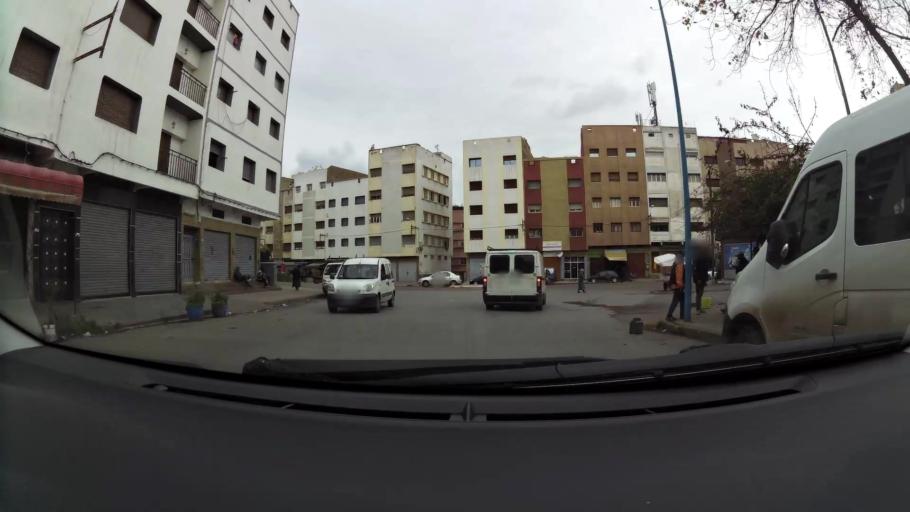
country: MA
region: Grand Casablanca
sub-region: Casablanca
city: Casablanca
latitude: 33.5727
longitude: -7.5599
